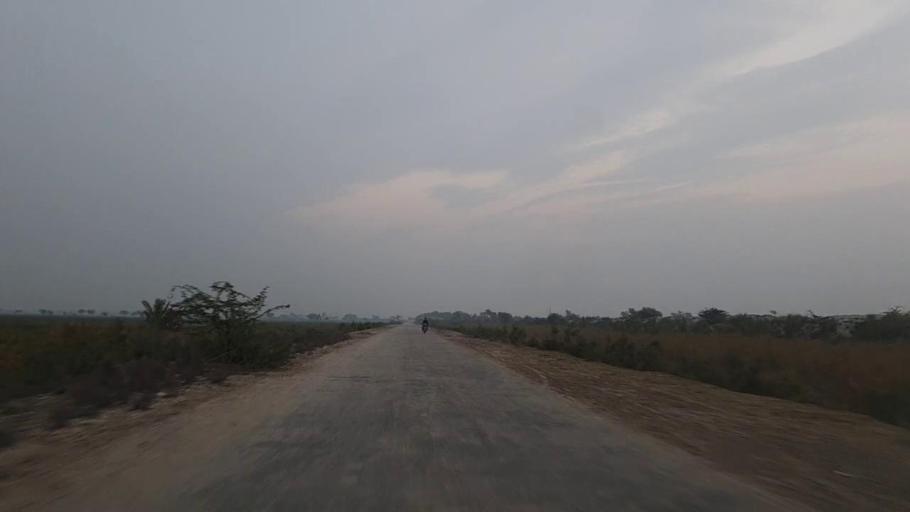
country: PK
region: Sindh
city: Jam Sahib
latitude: 26.3346
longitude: 68.5522
